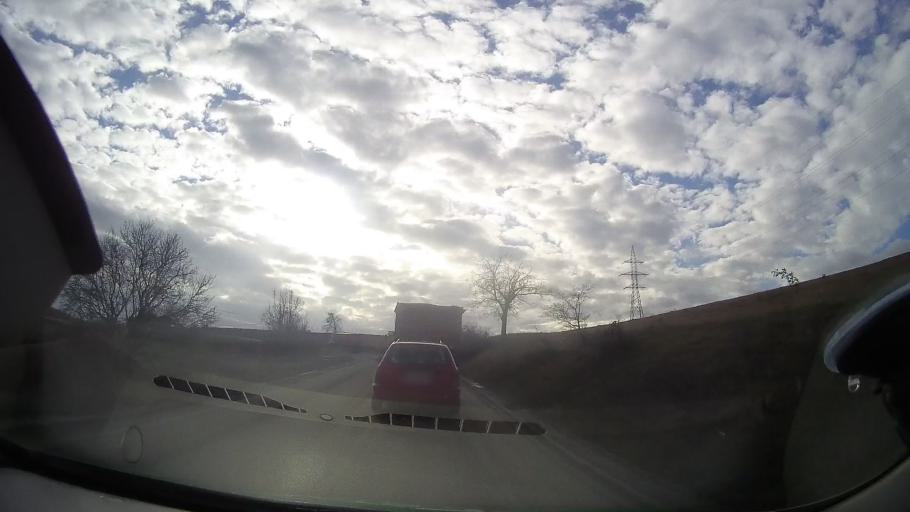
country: RO
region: Cluj
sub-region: Comuna Savadisla
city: Savadisla
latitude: 46.6544
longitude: 23.4529
